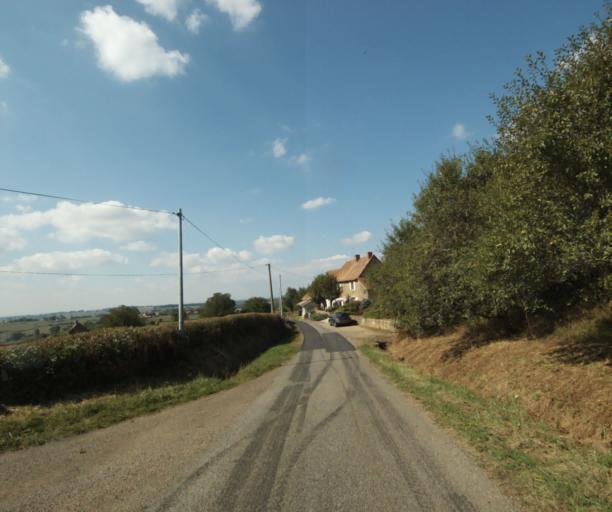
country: FR
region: Bourgogne
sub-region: Departement de Saone-et-Loire
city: Charolles
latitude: 46.3792
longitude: 4.2329
